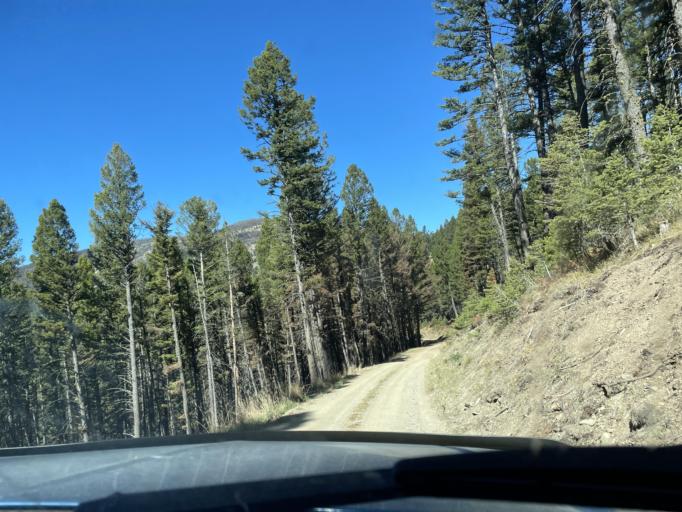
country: US
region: Montana
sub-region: Broadwater County
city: Townsend
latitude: 46.5068
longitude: -111.2834
